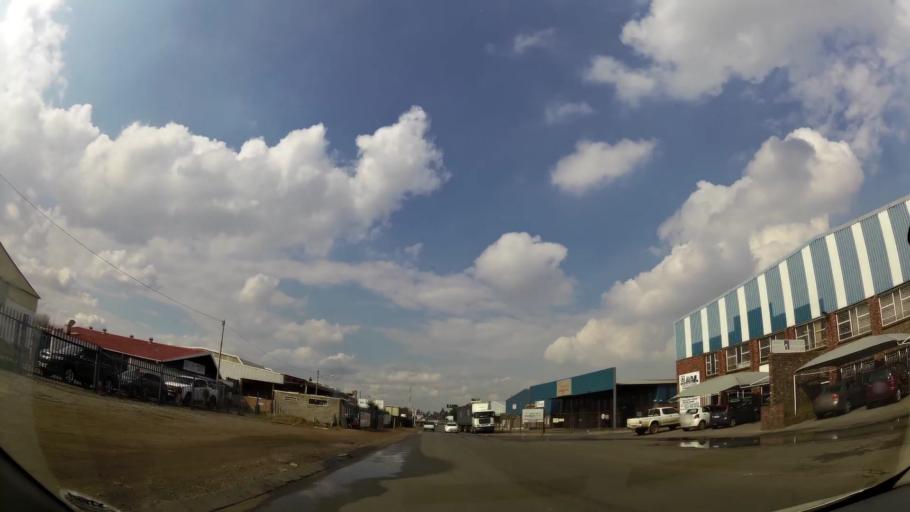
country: ZA
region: Gauteng
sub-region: Sedibeng District Municipality
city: Vereeniging
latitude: -26.6602
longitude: 27.9249
